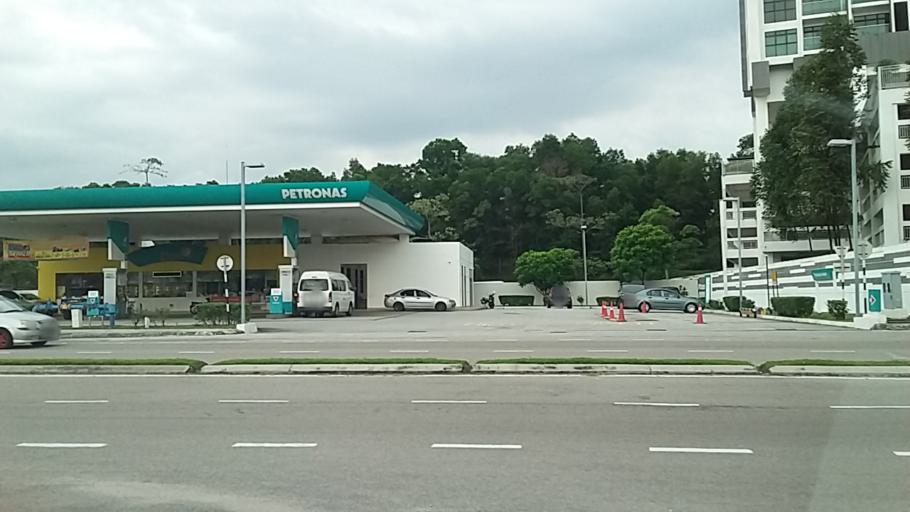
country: MY
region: Johor
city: Skudai
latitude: 1.4826
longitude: 103.6588
